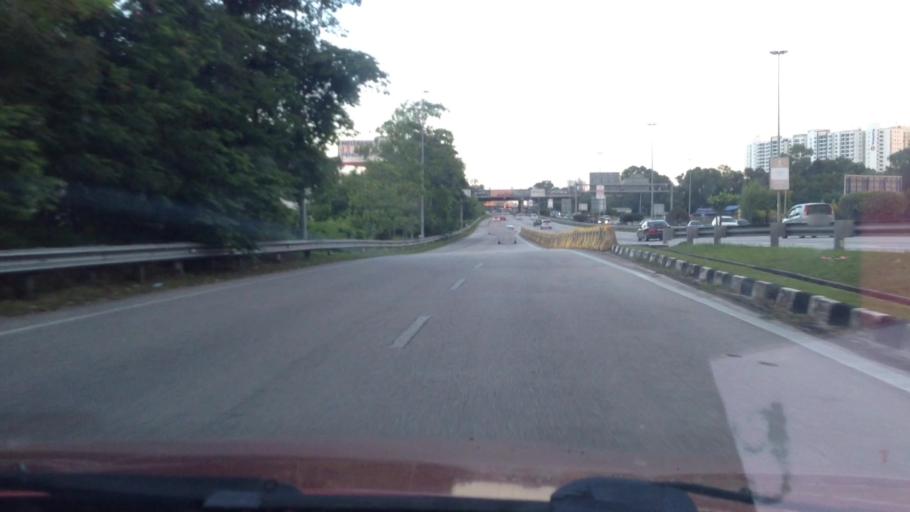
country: MY
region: Selangor
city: Shah Alam
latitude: 3.0978
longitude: 101.5486
